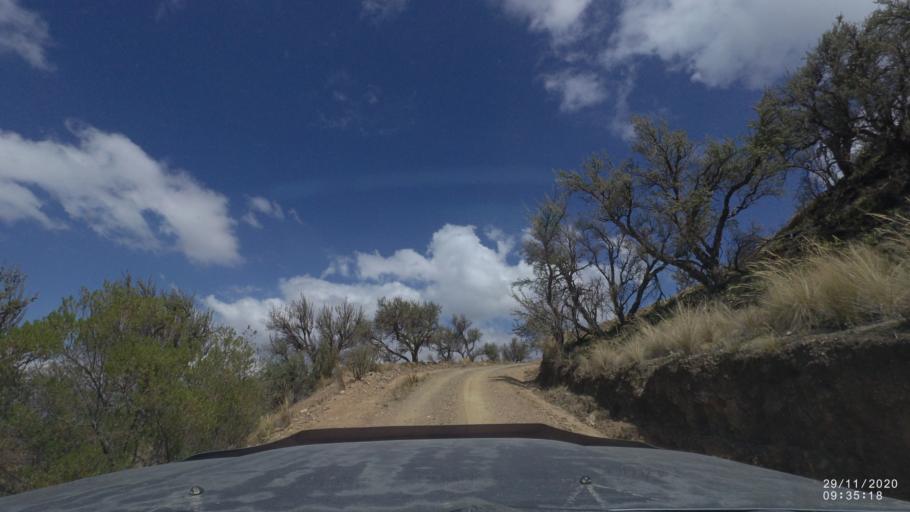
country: BO
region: Cochabamba
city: Cochabamba
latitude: -17.3106
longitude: -66.1890
